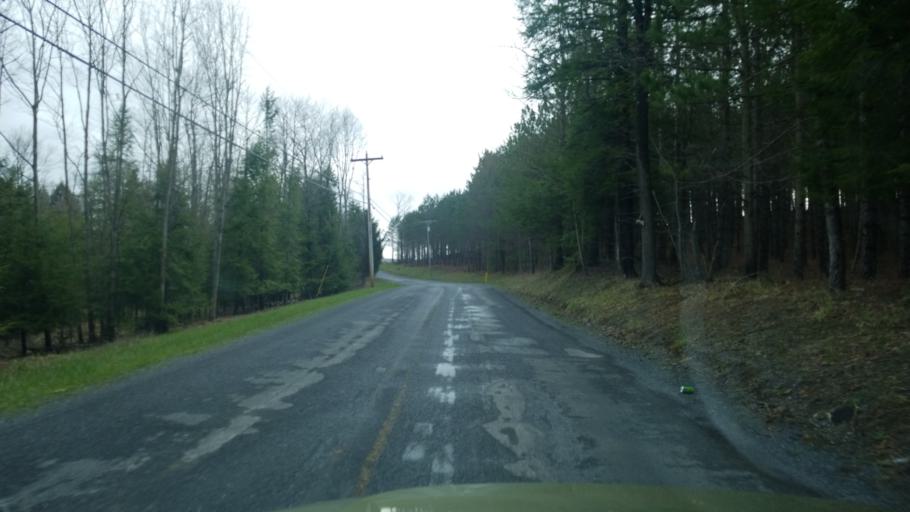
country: US
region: Pennsylvania
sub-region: Clearfield County
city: Clearfield
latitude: 41.0744
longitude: -78.4191
